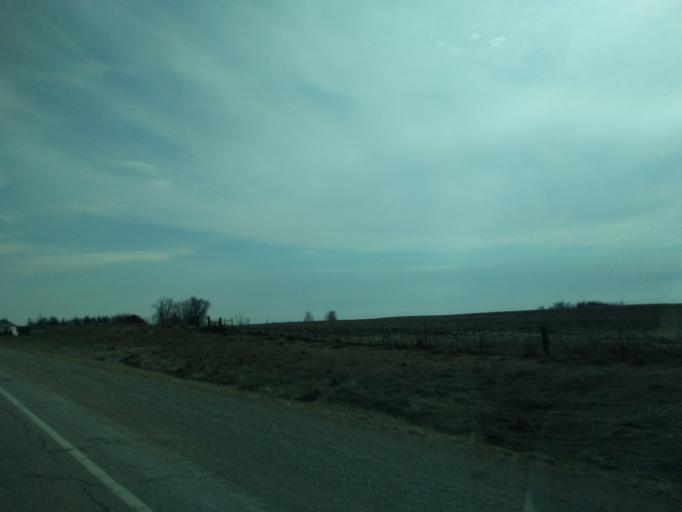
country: US
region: Iowa
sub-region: Allamakee County
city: Waukon
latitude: 43.2363
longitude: -91.4625
